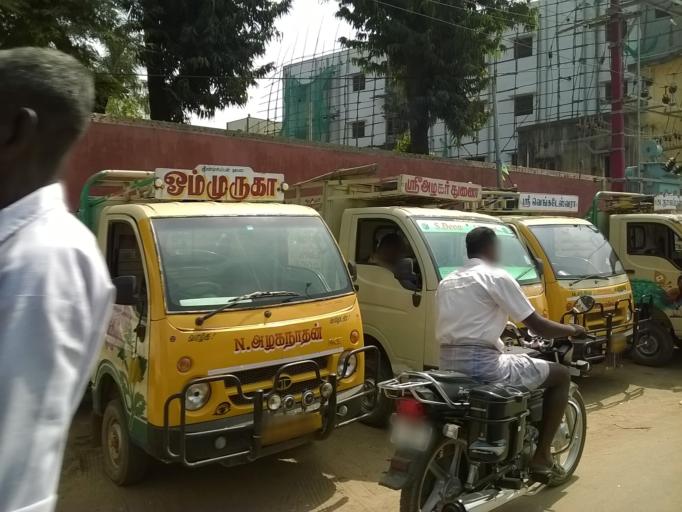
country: IN
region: Tamil Nadu
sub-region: Cuddalore
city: Panruti
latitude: 11.7717
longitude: 79.5512
